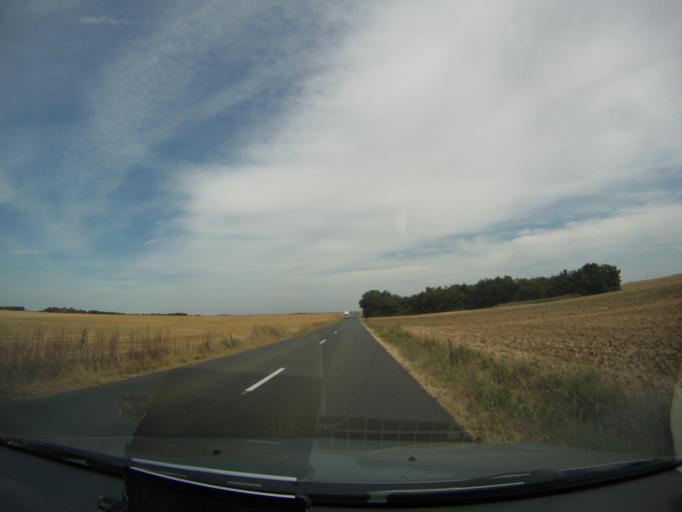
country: FR
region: Poitou-Charentes
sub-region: Departement de la Vienne
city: Moncontour
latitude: 46.8097
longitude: -0.0266
